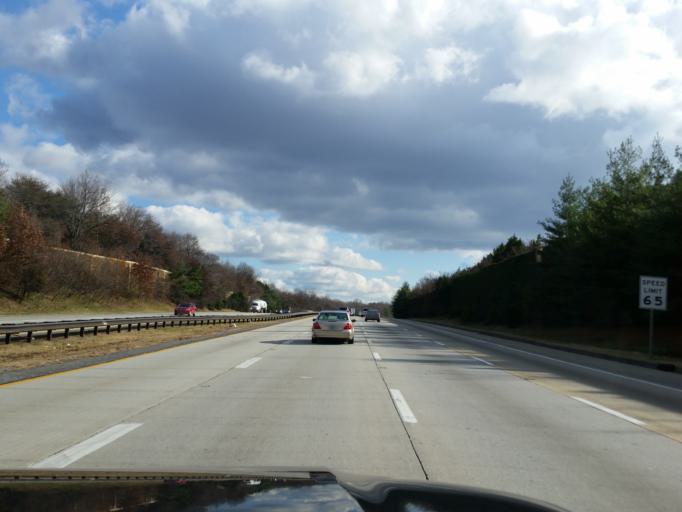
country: US
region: Maryland
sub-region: Prince George's County
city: Springdale
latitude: 38.9466
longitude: -76.8165
